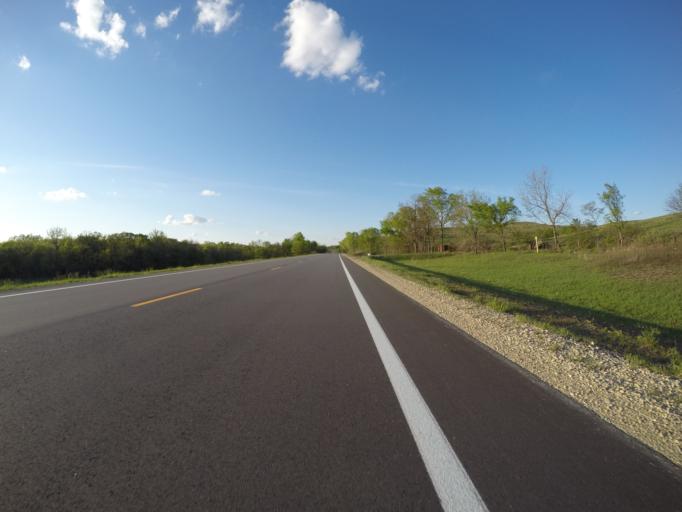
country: US
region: Kansas
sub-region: Riley County
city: Manhattan
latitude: 39.2877
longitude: -96.5576
